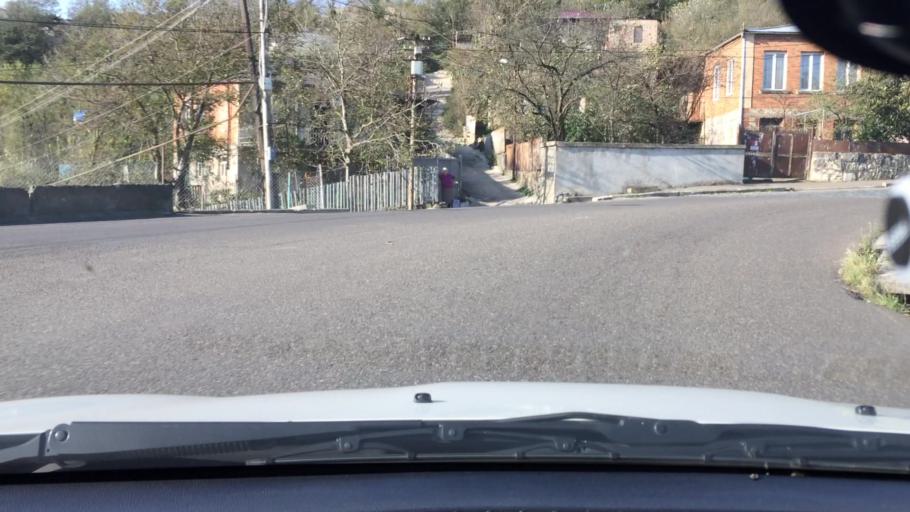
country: GE
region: Imereti
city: Kutaisi
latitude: 42.2631
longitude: 42.7227
